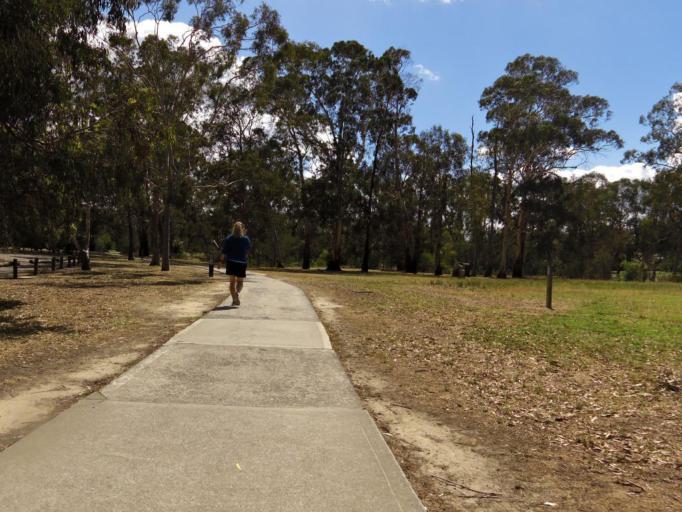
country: AU
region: Victoria
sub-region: Nillumbik
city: Diamond Creek
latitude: -37.6760
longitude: 145.1515
